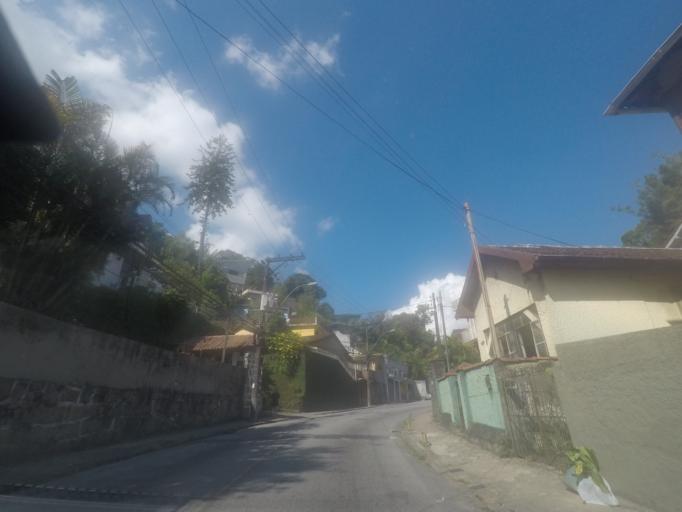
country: BR
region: Rio de Janeiro
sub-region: Petropolis
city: Petropolis
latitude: -22.5165
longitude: -43.1912
